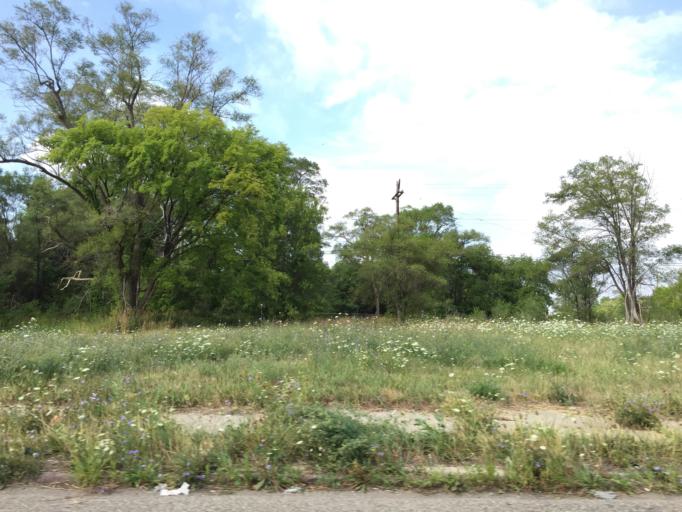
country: US
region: Michigan
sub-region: Wayne County
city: Hamtramck
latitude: 42.3631
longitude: -83.0391
